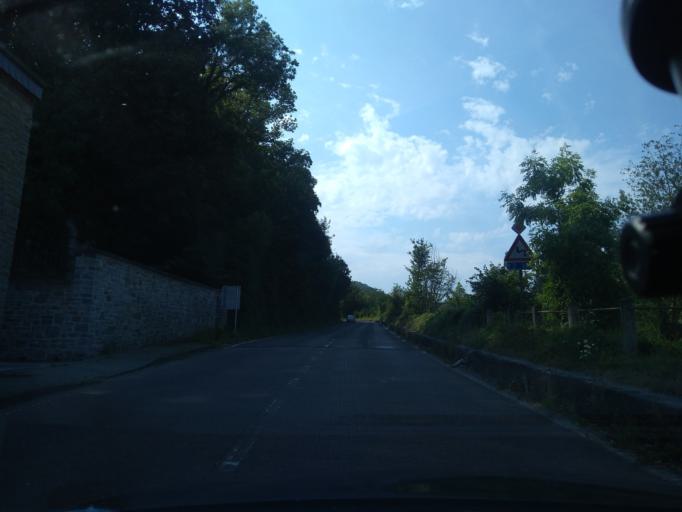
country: BE
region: Wallonia
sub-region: Province de Namur
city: Dinant
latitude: 50.2387
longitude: 4.9050
